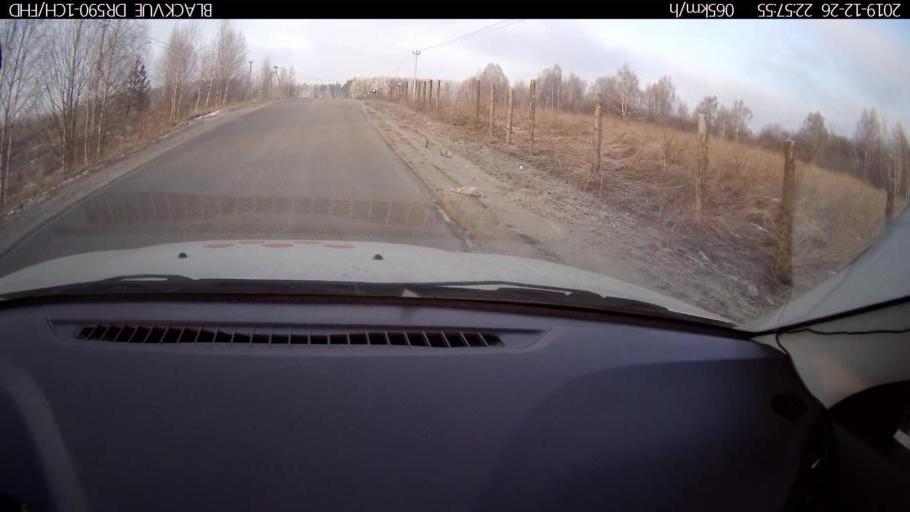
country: RU
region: Nizjnij Novgorod
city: Burevestnik
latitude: 56.1542
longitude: 43.7121
